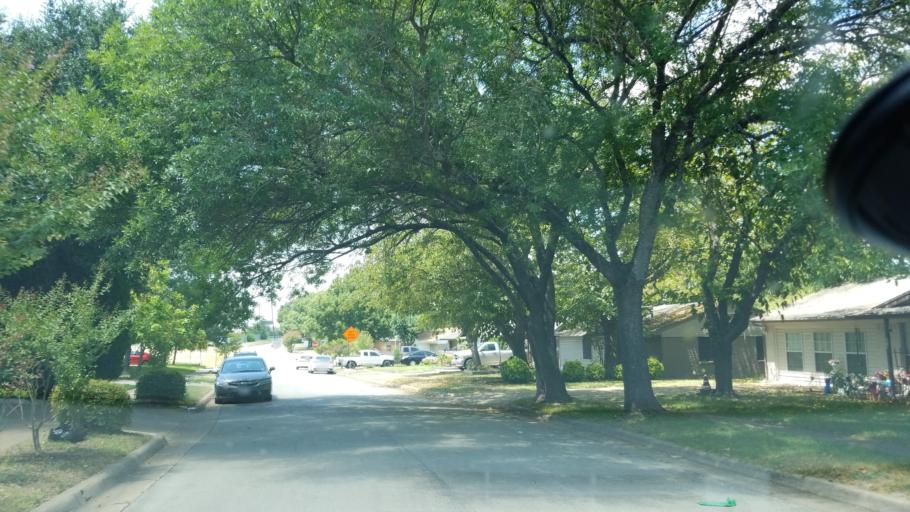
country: US
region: Texas
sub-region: Dallas County
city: Duncanville
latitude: 32.6643
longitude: -96.8980
